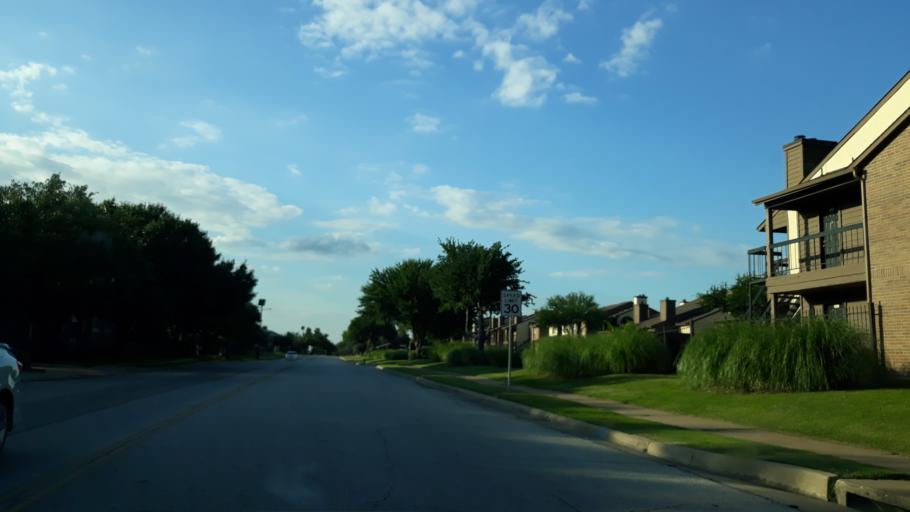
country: US
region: Texas
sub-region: Dallas County
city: Irving
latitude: 32.8571
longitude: -96.9964
